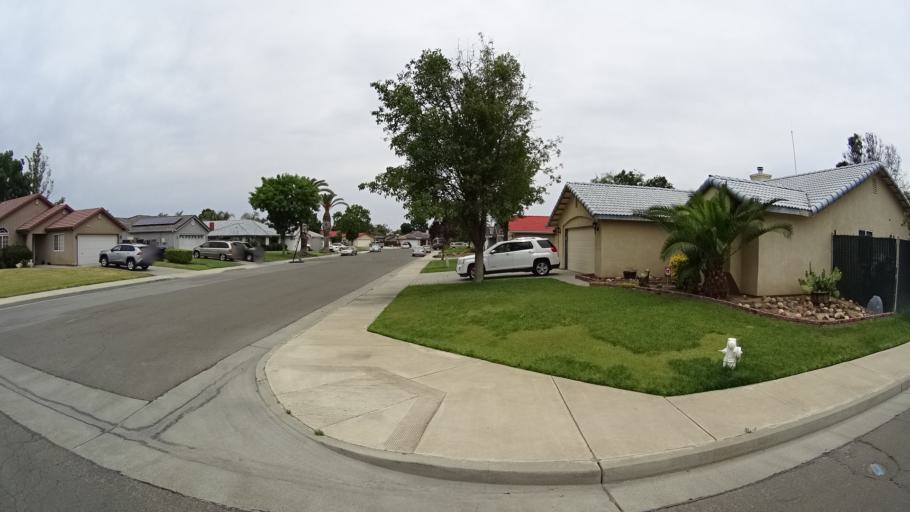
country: US
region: California
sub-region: Kings County
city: Hanford
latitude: 36.3553
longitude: -119.6333
